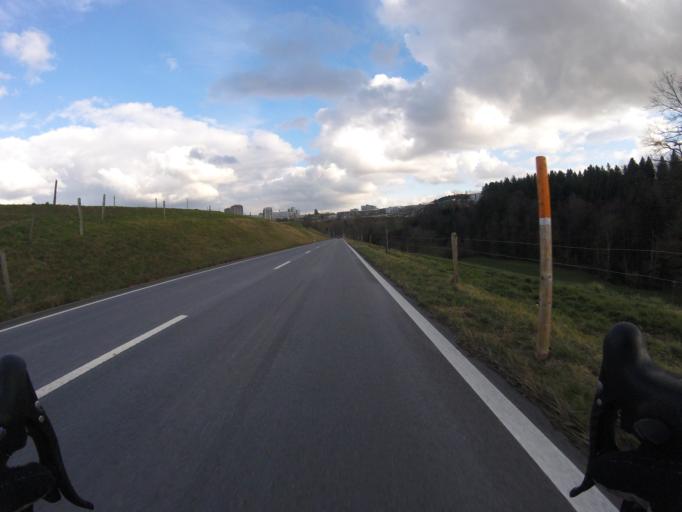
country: CH
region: Bern
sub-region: Bern-Mittelland District
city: Wohlen
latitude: 46.9477
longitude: 7.3662
